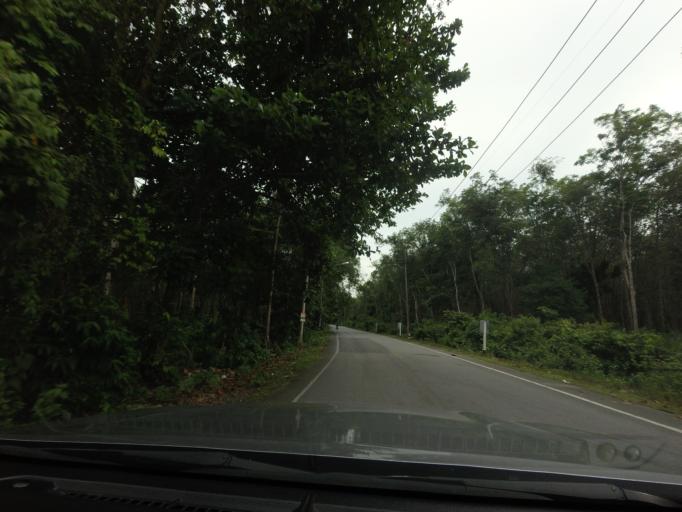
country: TH
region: Yala
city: Raman
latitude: 6.4342
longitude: 101.4542
